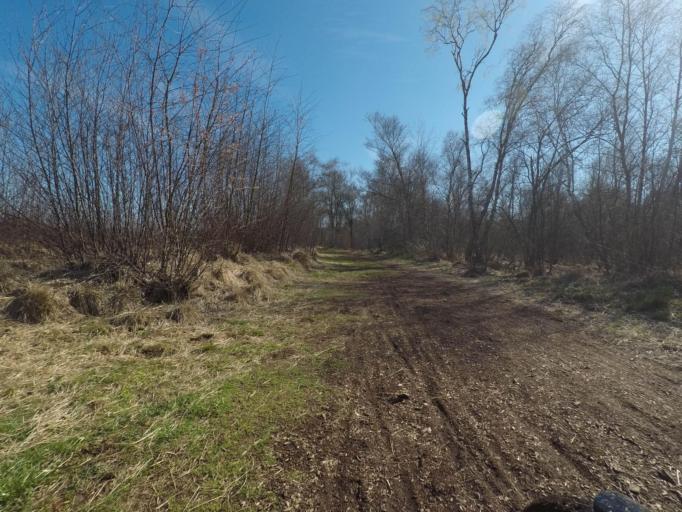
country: DE
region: Hamburg
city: Langenhorn
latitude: 53.6527
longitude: 9.9729
